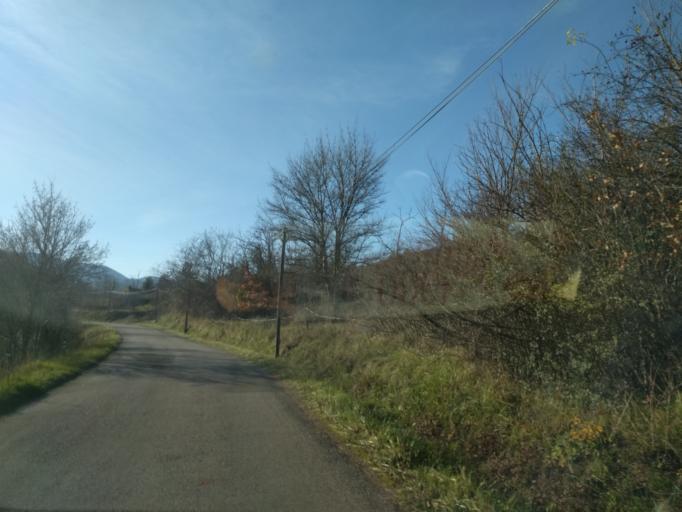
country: FR
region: Languedoc-Roussillon
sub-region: Departement de l'Aude
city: Quillan
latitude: 42.9065
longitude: 2.1843
